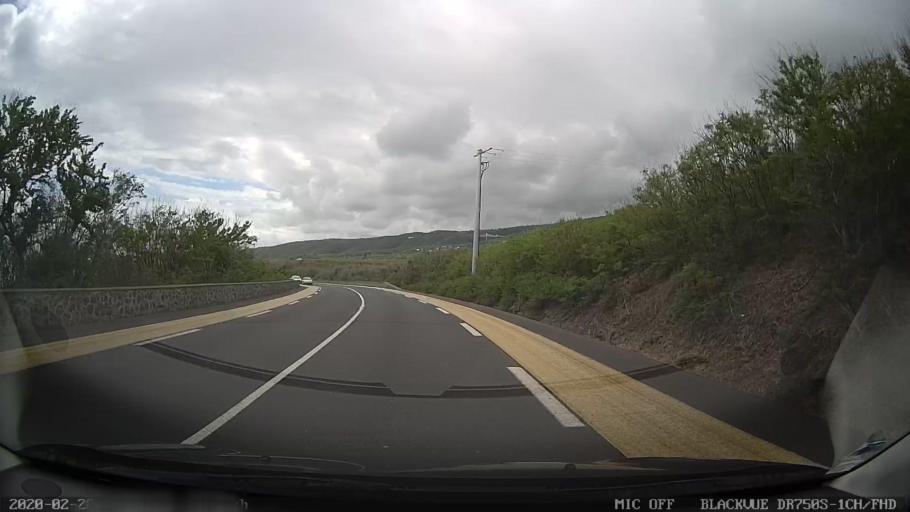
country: RE
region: Reunion
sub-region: Reunion
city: Saint-Leu
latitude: -21.1323
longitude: 55.2722
